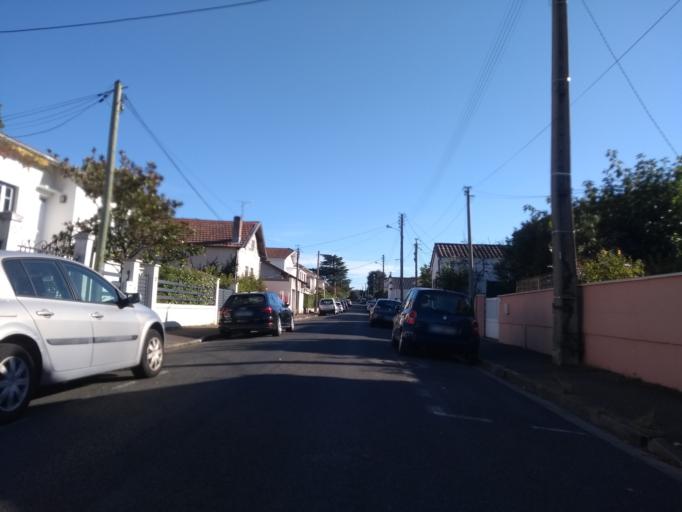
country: FR
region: Aquitaine
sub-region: Departement de la Gironde
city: Talence
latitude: 44.8144
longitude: -0.5983
